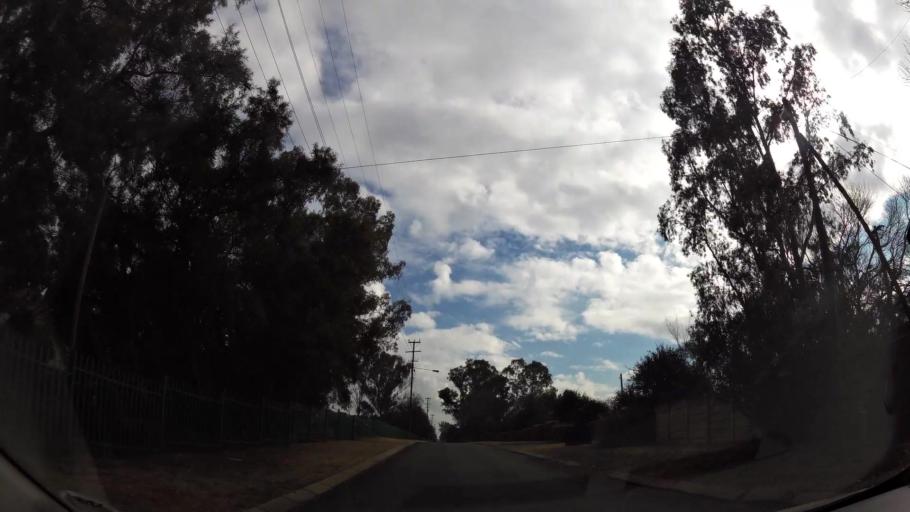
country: ZA
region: Gauteng
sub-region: Sedibeng District Municipality
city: Meyerton
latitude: -26.5891
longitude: 28.0154
